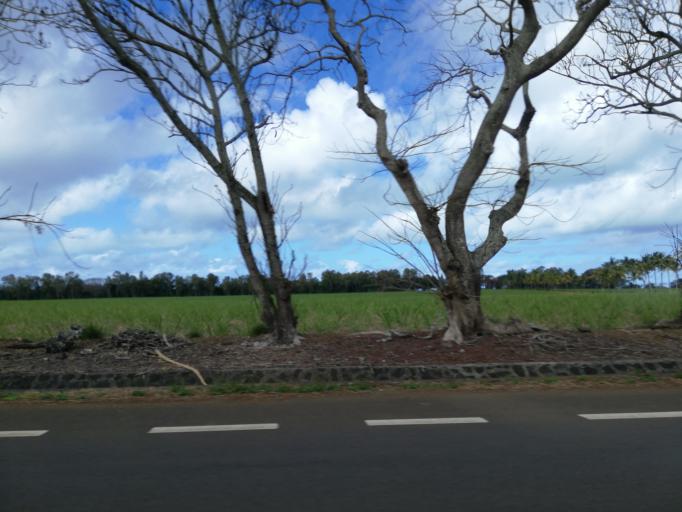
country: MU
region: Grand Port
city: Mahebourg
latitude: -20.3810
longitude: 57.6979
